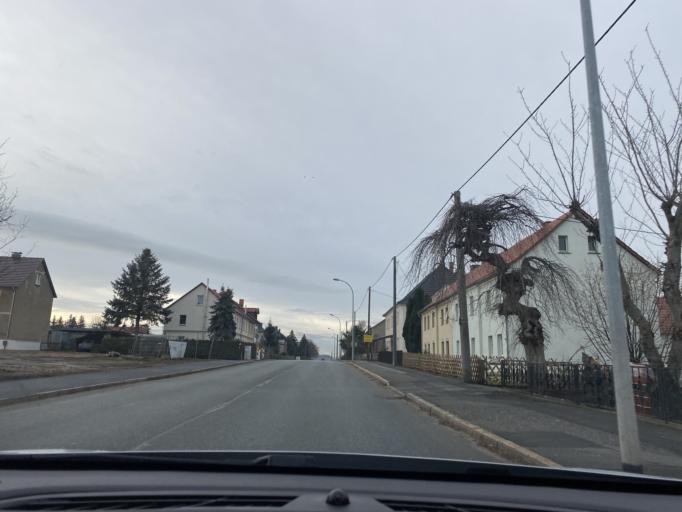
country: DE
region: Saxony
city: Reichenbach
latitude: 51.1383
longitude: 14.7931
